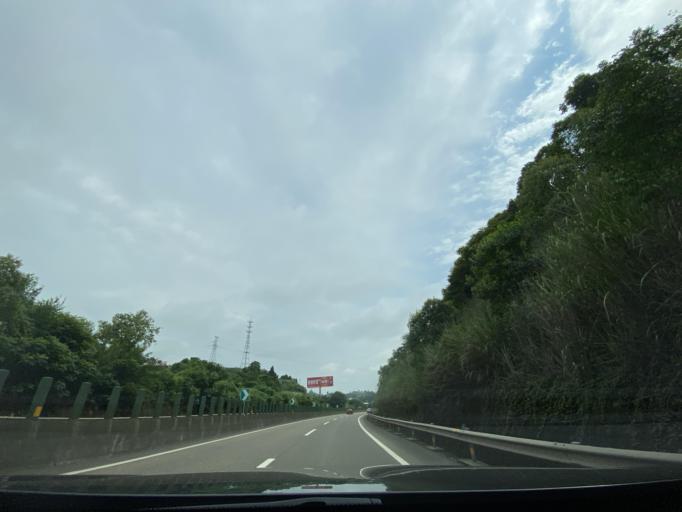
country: CN
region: Sichuan
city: Chonglong
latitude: 29.7137
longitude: 104.9410
